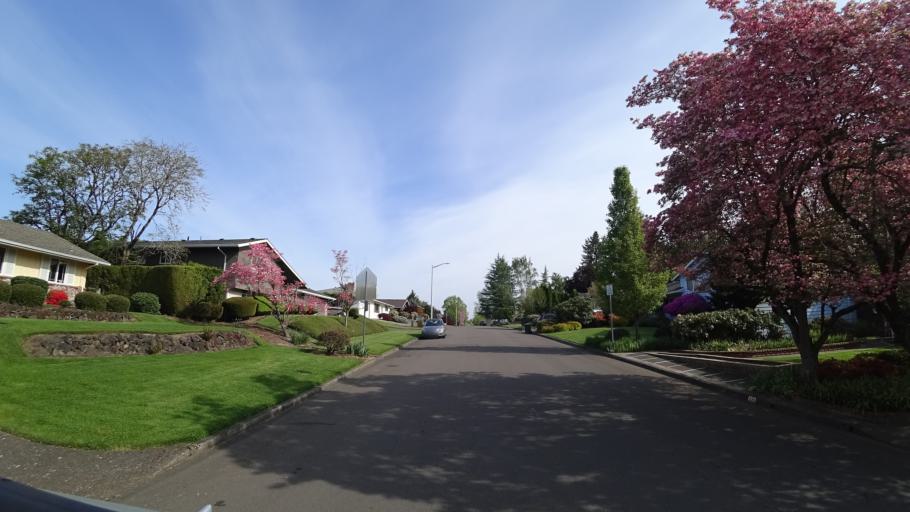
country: US
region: Oregon
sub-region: Washington County
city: Hillsboro
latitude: 45.5235
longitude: -122.9648
